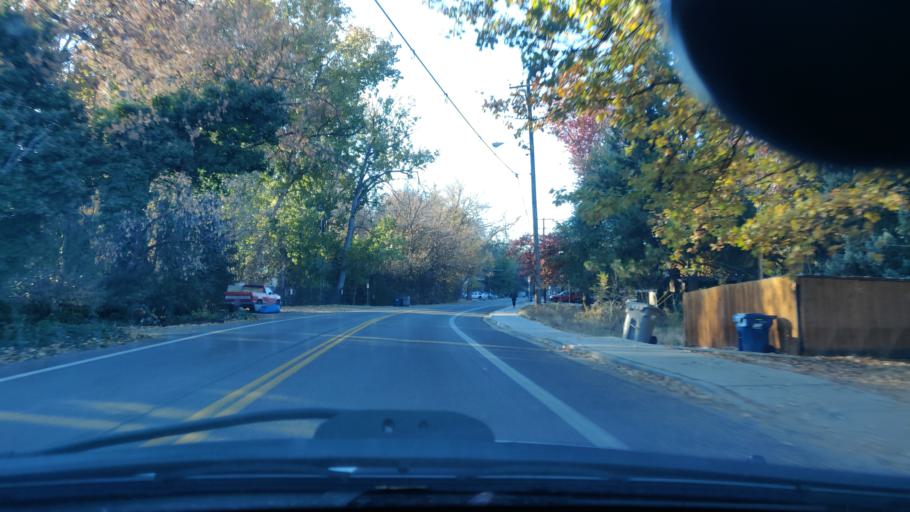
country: US
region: Idaho
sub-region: Ada County
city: Boise
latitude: 43.6007
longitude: -116.2083
